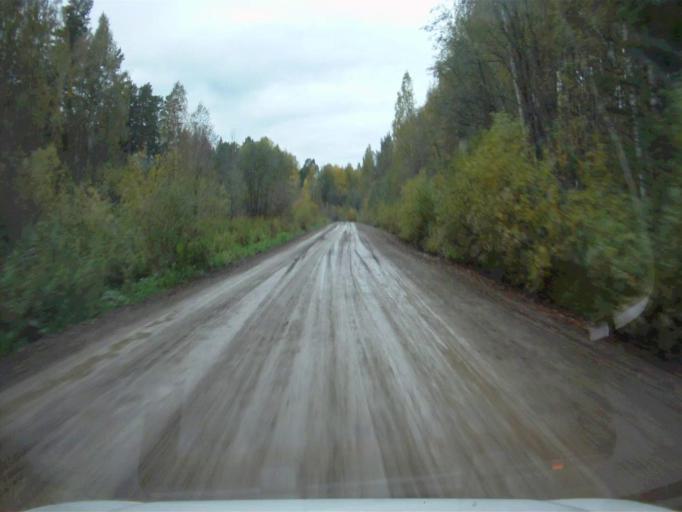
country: RU
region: Chelyabinsk
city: Nyazepetrovsk
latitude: 56.0998
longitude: 59.3914
